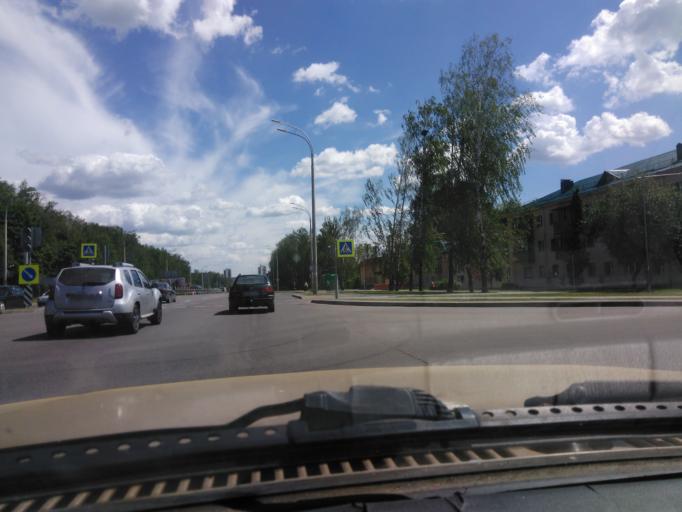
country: BY
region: Mogilev
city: Buynichy
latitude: 53.9304
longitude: 30.2634
